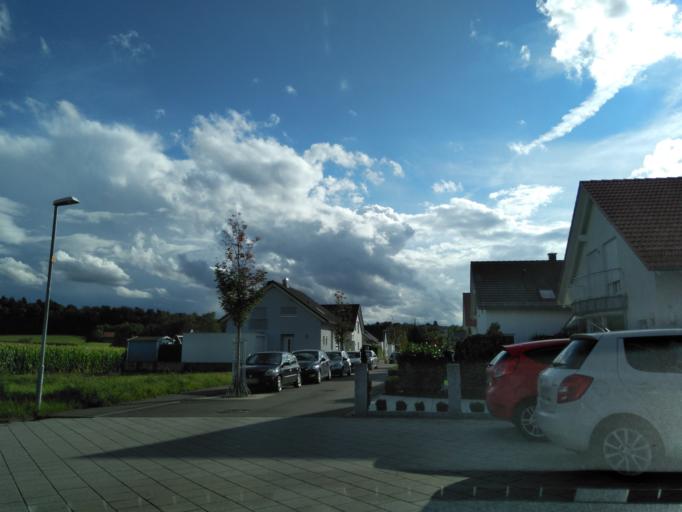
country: DE
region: Baden-Wuerttemberg
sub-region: Regierungsbezirk Stuttgart
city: Sersheim
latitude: 48.9582
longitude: 9.0218
